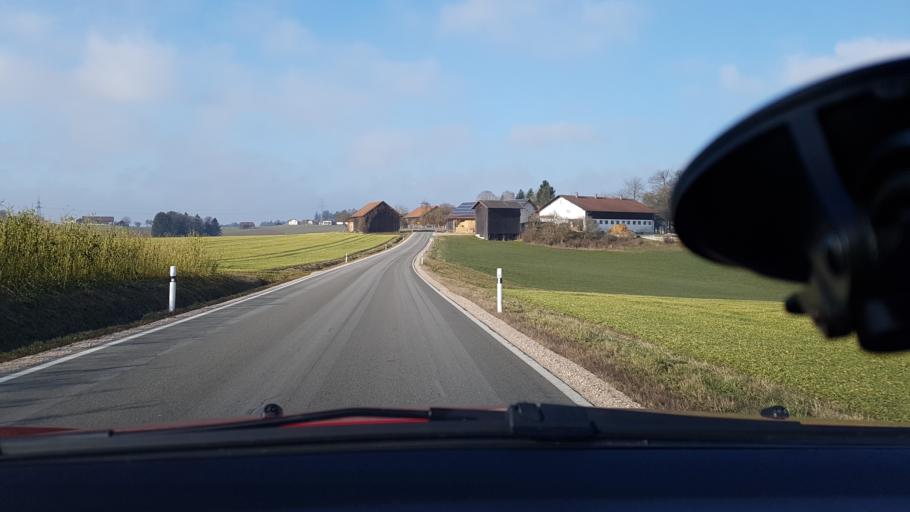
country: DE
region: Bavaria
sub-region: Lower Bavaria
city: Wittibreut
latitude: 48.3364
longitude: 12.9690
